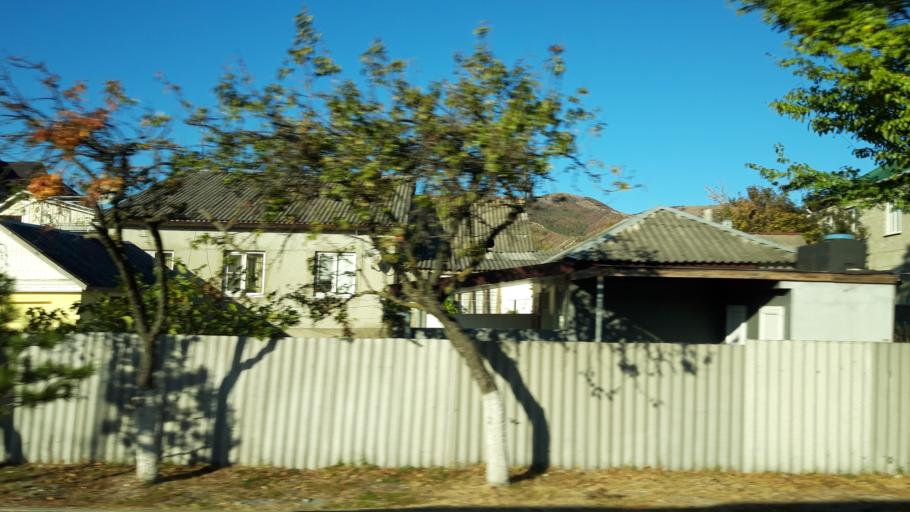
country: RU
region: Krasnodarskiy
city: Kabardinka
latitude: 44.6482
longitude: 37.9492
